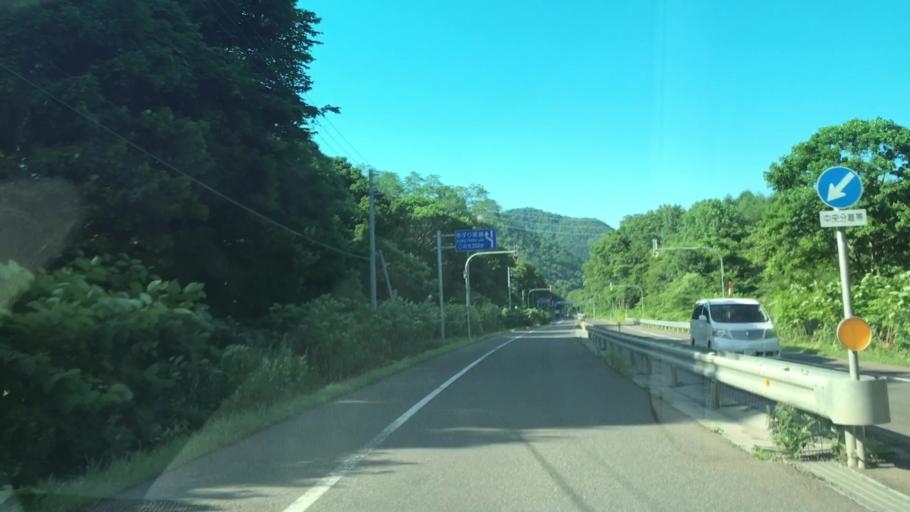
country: JP
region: Hokkaido
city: Iwanai
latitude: 43.0098
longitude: 140.6654
